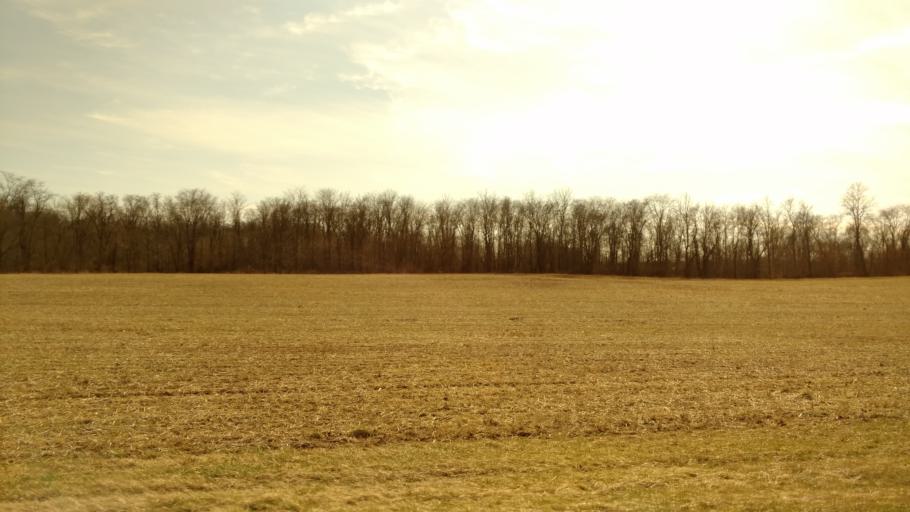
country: US
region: Ohio
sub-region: Hardin County
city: Kenton
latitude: 40.5847
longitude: -83.5004
